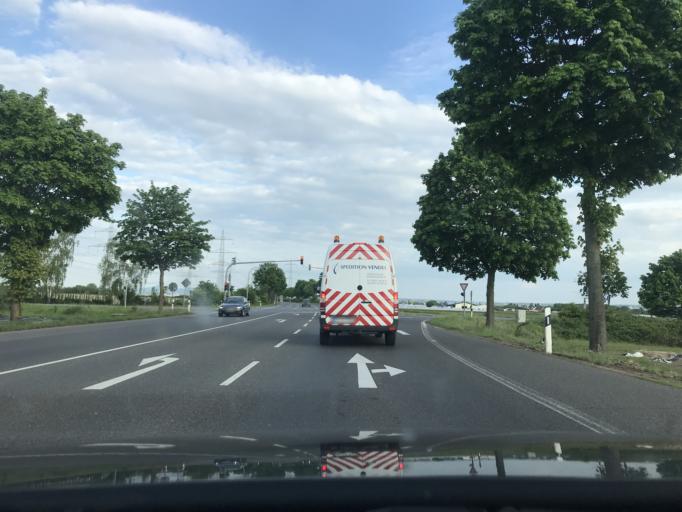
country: DE
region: North Rhine-Westphalia
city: Bornheim
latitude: 50.7689
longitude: 7.0041
